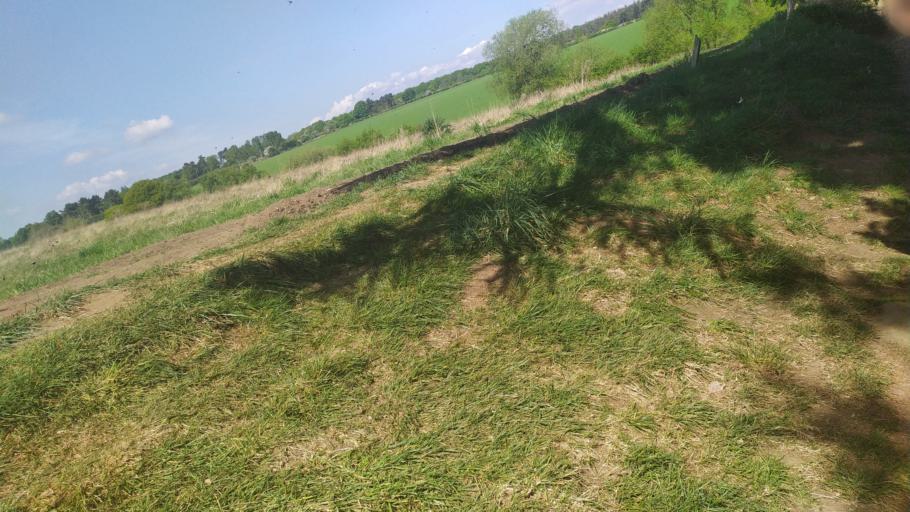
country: GB
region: England
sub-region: City and Borough of Leeds
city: Chapel Allerton
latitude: 53.8691
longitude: -1.5611
